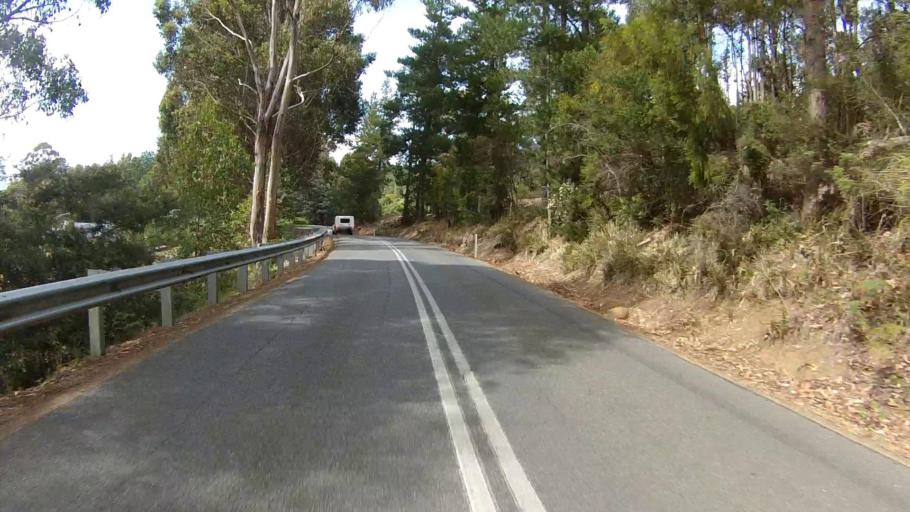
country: AU
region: Tasmania
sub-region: Kingborough
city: Kettering
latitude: -43.2036
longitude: 147.2541
